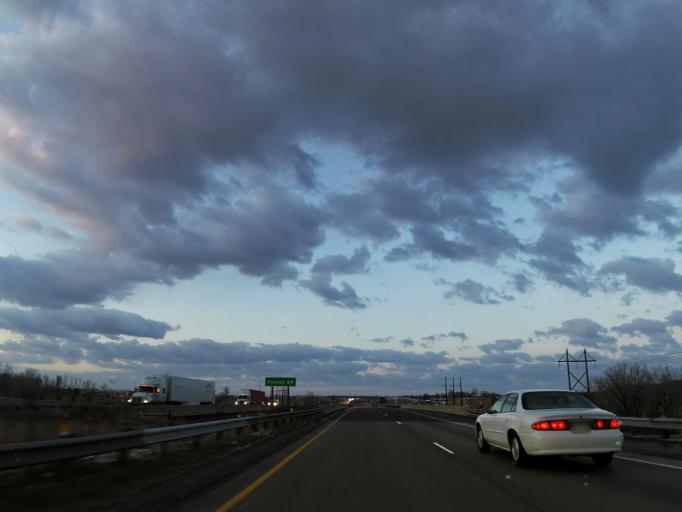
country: US
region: Minnesota
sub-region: Dakota County
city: Lakeville
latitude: 44.6533
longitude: -93.2948
